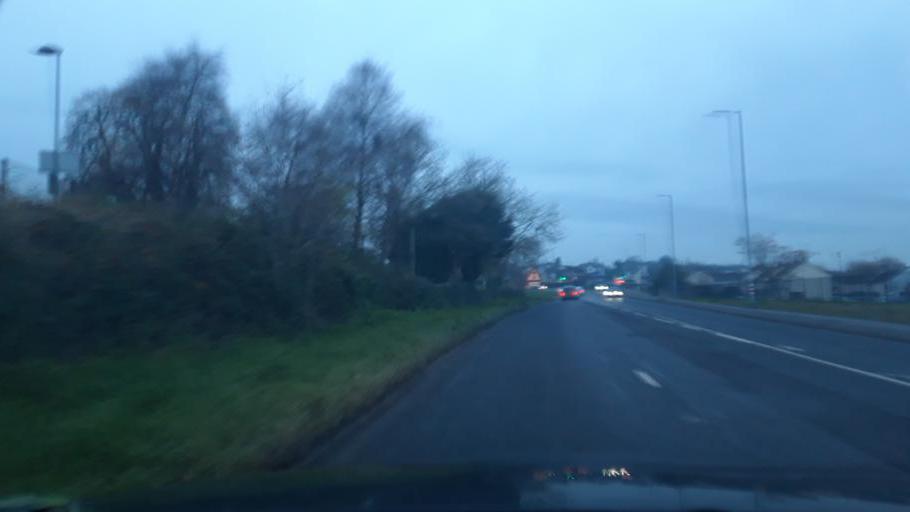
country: GB
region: Northern Ireland
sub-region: Newry and Mourne District
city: Newry
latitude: 54.1831
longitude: -6.3548
